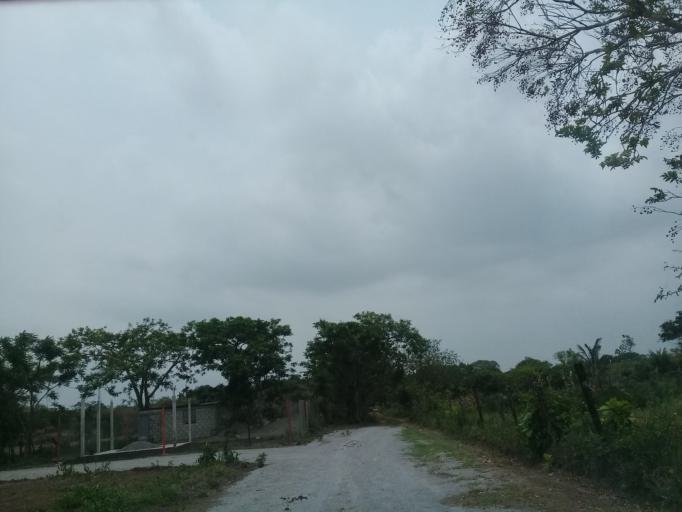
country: MX
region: Veracruz
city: El Tejar
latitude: 19.0429
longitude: -96.1672
